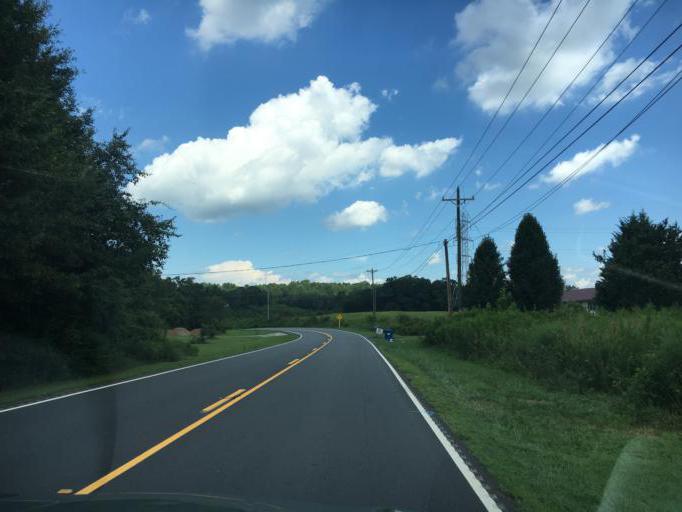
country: US
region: South Carolina
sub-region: Spartanburg County
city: Duncan
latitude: 34.9233
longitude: -82.1440
